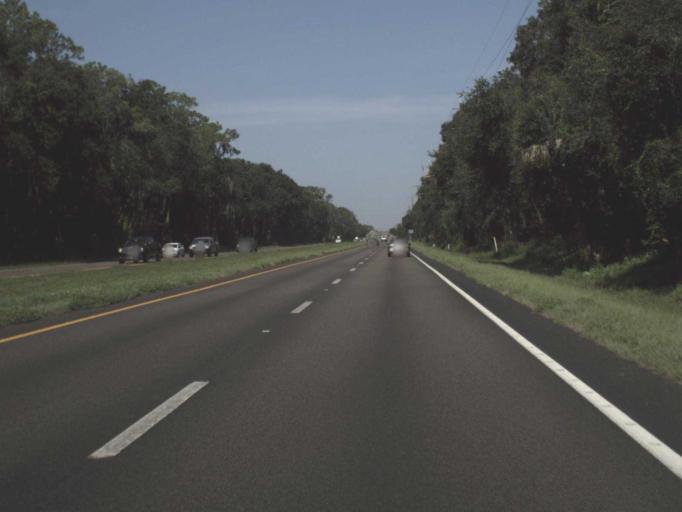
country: US
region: Florida
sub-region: Hillsborough County
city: Valrico
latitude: 27.9378
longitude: -82.1979
